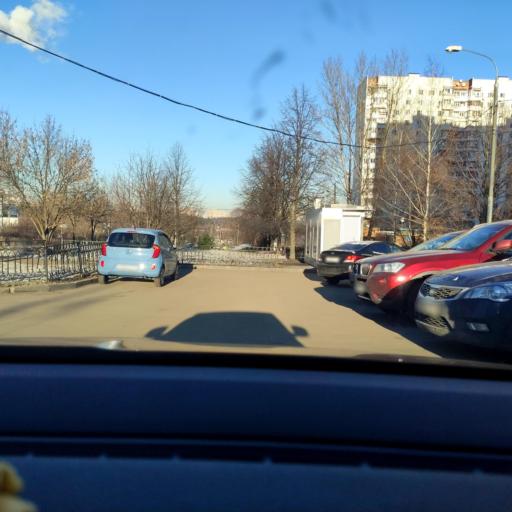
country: RU
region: Moskovskaya
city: Bol'shaya Setun'
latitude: 55.7668
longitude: 37.4073
